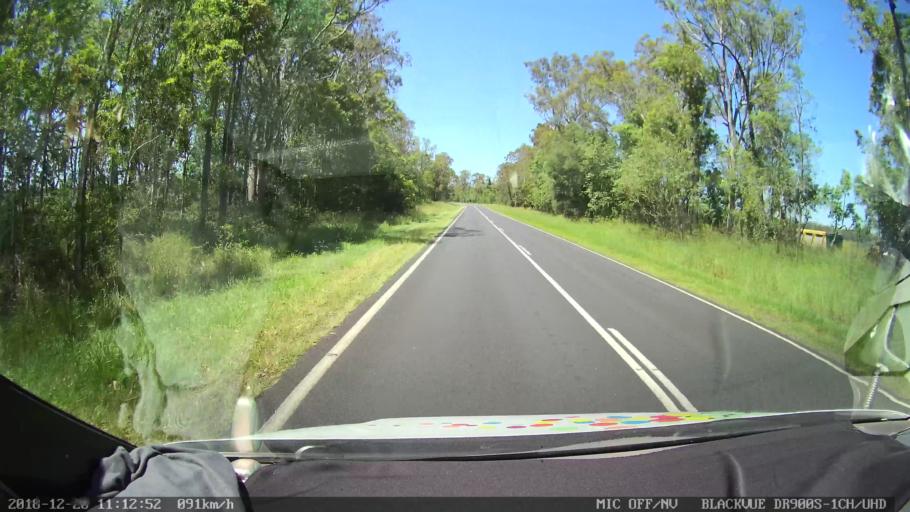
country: AU
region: New South Wales
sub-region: Richmond Valley
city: Casino
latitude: -28.9799
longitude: 153.0097
